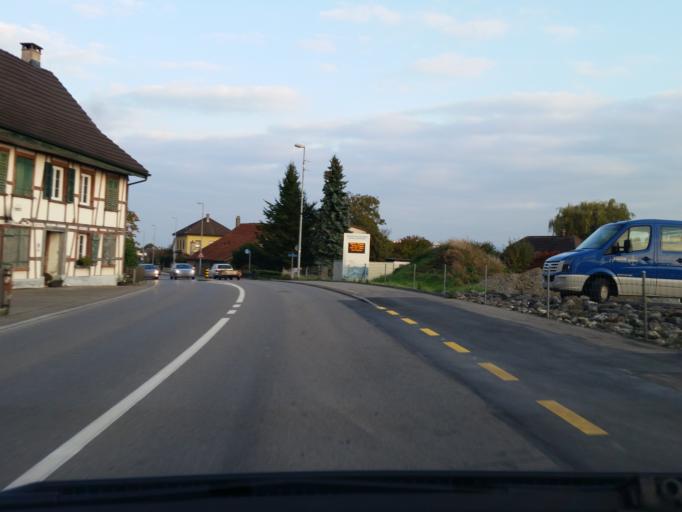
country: CH
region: Thurgau
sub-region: Arbon District
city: Salmsach
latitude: 47.5733
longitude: 9.3625
